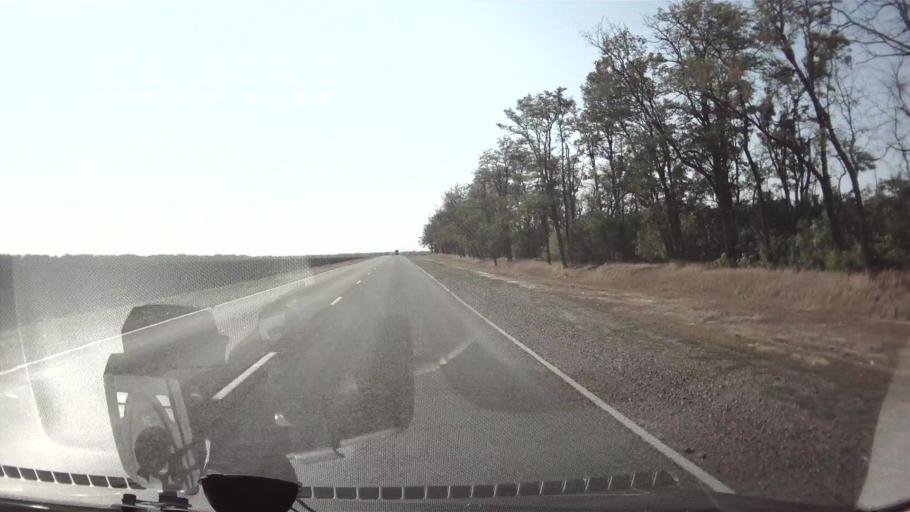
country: RU
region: Krasnodarskiy
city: Belaya Glina
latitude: 46.0353
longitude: 40.7988
